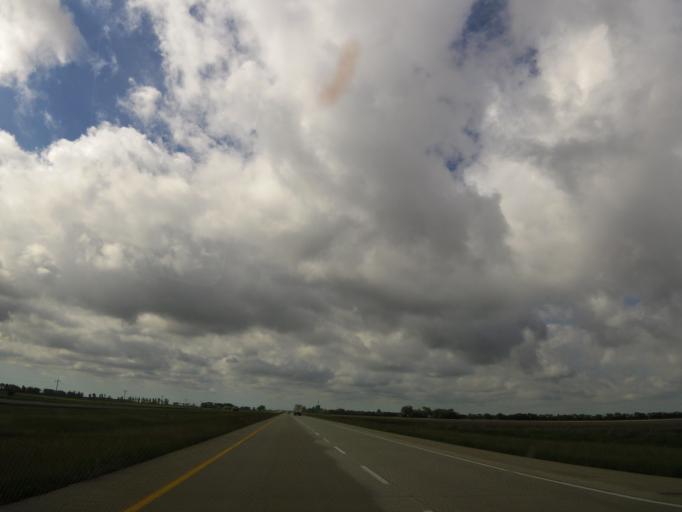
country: US
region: North Dakota
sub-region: Walsh County
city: Grafton
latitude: 48.2200
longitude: -97.1895
